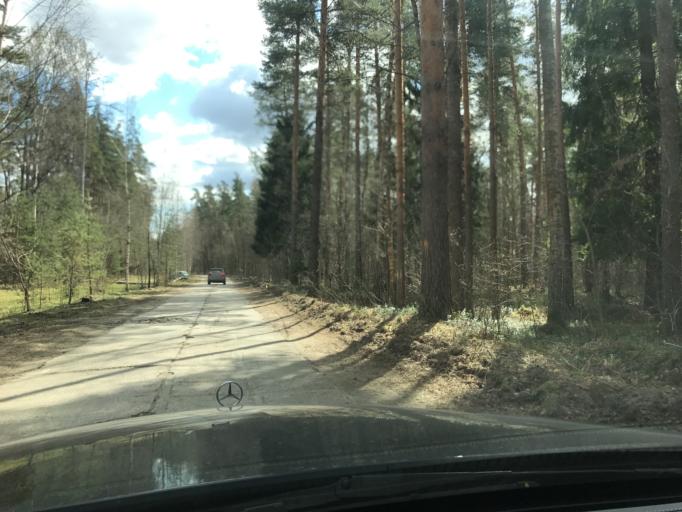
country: RU
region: Moskovskaya
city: Vereya
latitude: 55.8405
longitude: 39.1078
